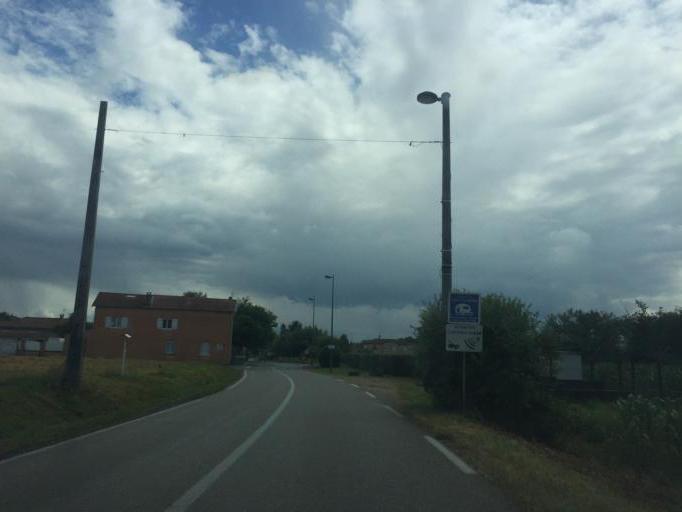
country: FR
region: Rhone-Alpes
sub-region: Departement du Rhone
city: Jons
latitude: 45.7955
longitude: 5.1068
